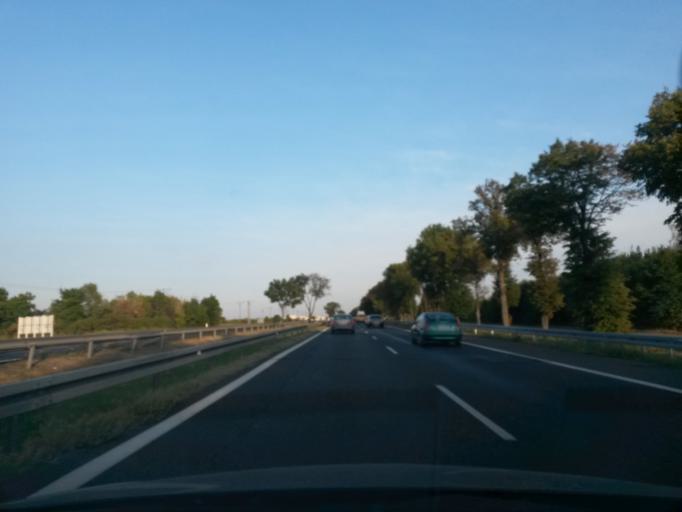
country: PL
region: Masovian Voivodeship
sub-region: Powiat nowodworski
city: Nowy Dwor Mazowiecki
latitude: 52.3862
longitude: 20.7457
